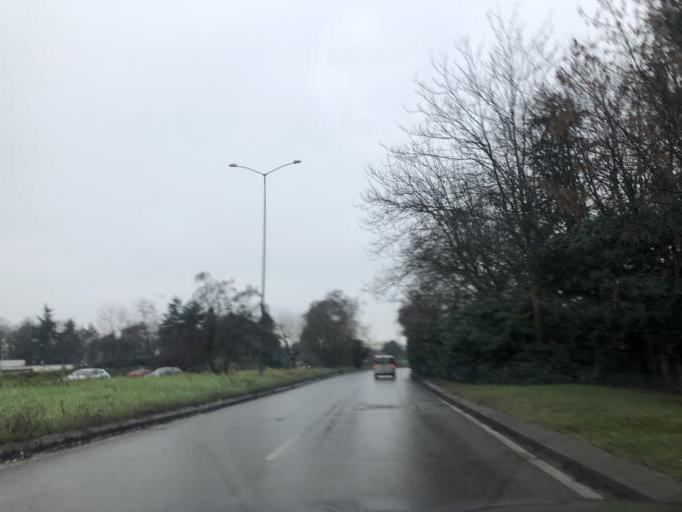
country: IT
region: Emilia-Romagna
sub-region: Provincia di Modena
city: Modena
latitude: 44.6367
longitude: 10.8935
